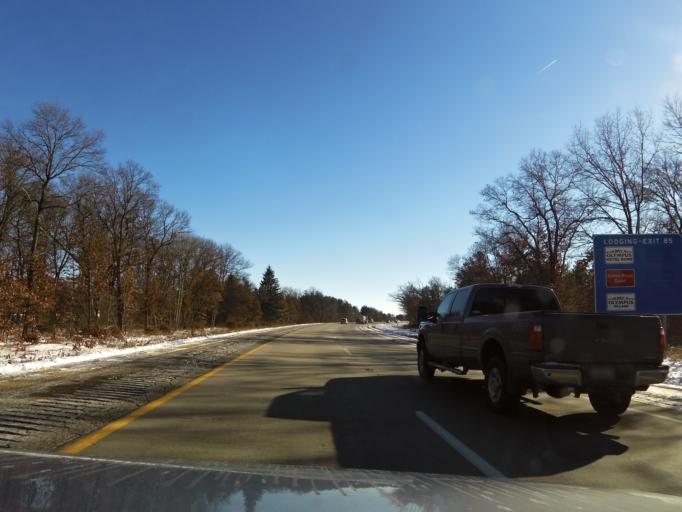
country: US
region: Wisconsin
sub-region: Columbia County
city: Wisconsin Dells
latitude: 43.6644
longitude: -89.8155
